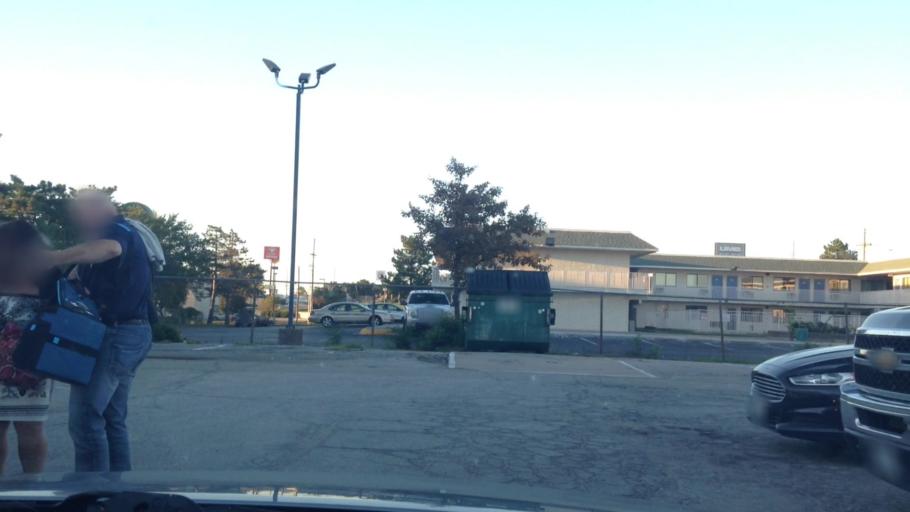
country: US
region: Missouri
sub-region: Platte County
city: Weatherby Lake
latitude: 39.2431
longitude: -94.6599
